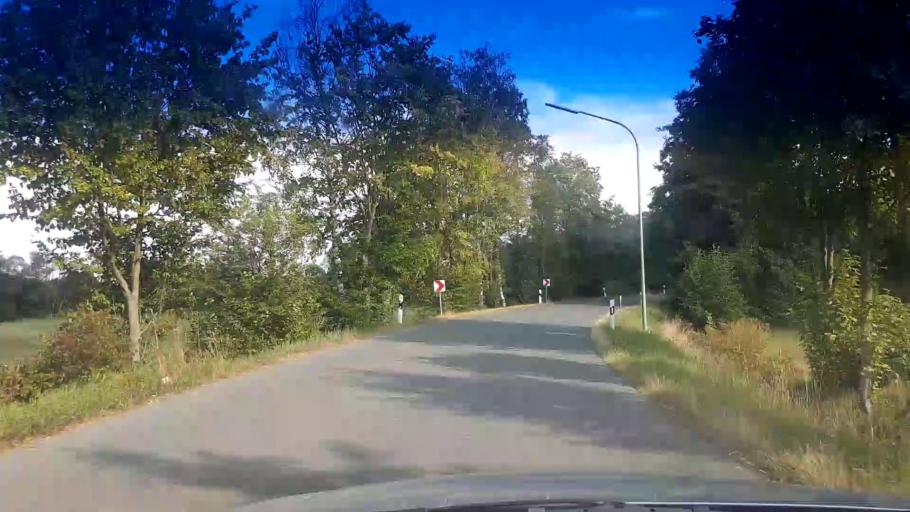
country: DE
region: Bavaria
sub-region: Upper Palatinate
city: Waldsassen
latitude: 50.0247
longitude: 12.3421
